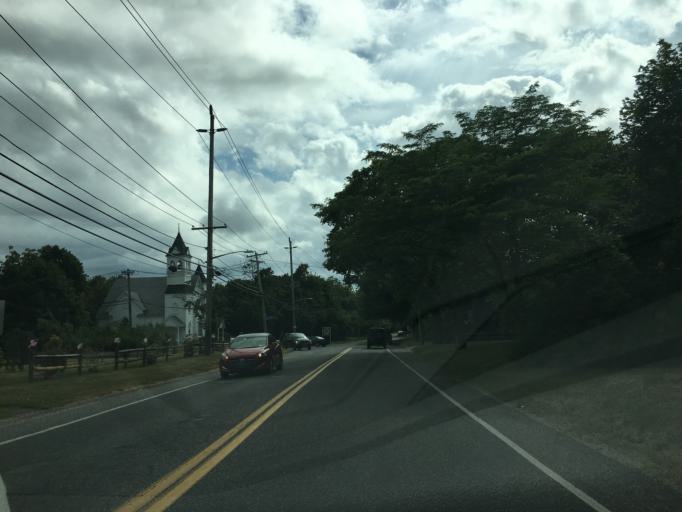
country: US
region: New York
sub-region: Suffolk County
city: Northville
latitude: 40.9705
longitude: -72.6180
